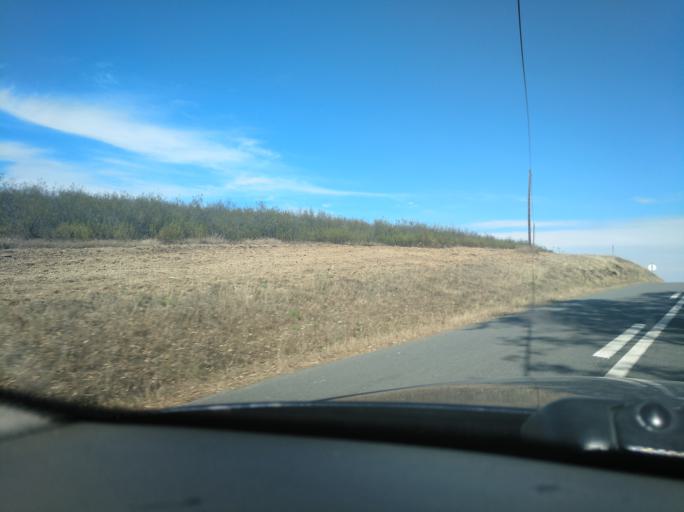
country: PT
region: Beja
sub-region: Mertola
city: Mertola
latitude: 37.6217
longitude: -7.7387
